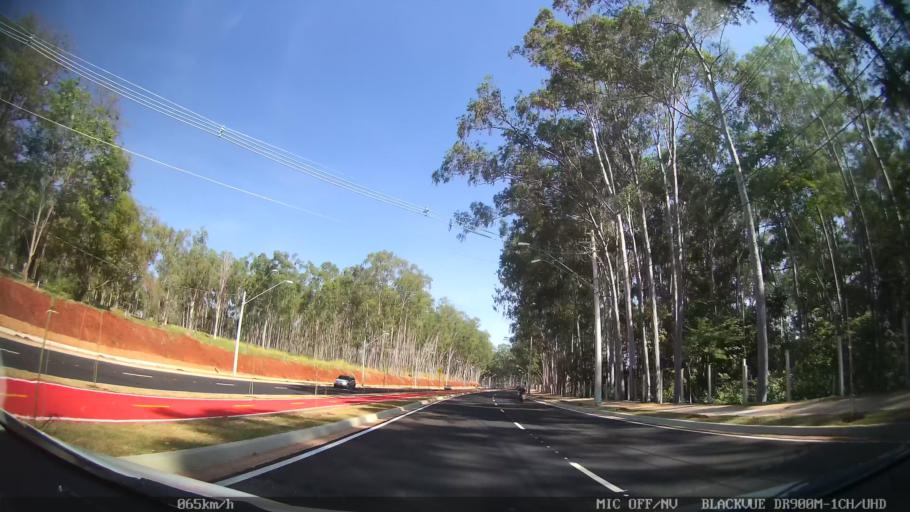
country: BR
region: Sao Paulo
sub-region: Ribeirao Preto
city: Ribeirao Preto
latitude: -21.2077
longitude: -47.8314
